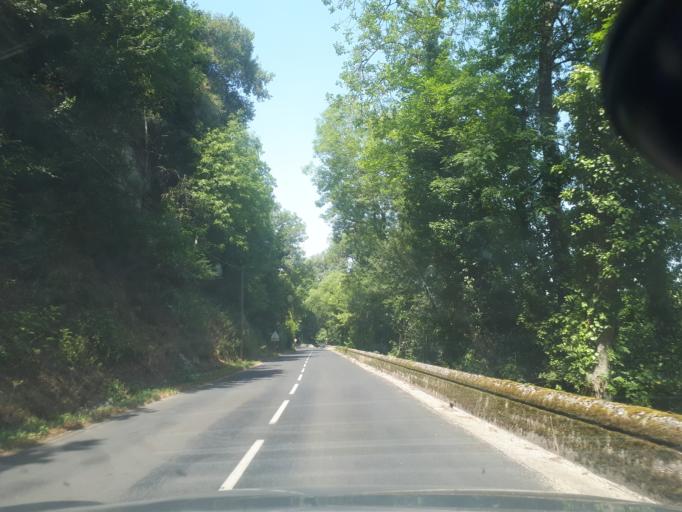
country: FR
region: Midi-Pyrenees
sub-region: Departement du Lot
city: Souillac
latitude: 44.8704
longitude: 1.4161
